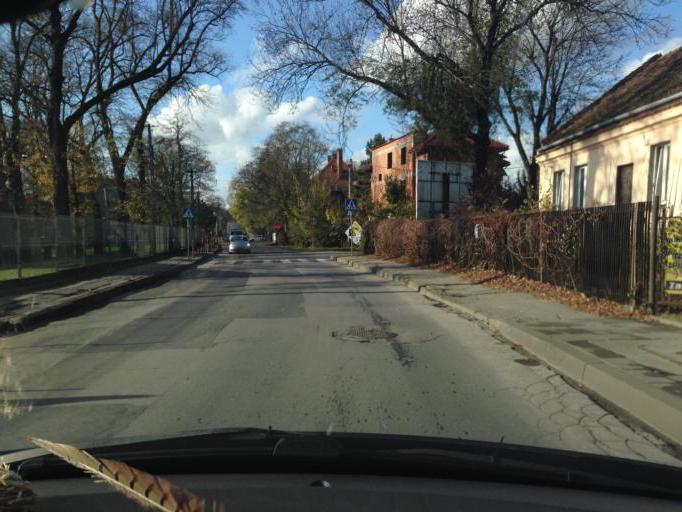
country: PL
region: Lesser Poland Voivodeship
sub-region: Powiat krakowski
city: Rzaska
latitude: 50.0645
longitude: 19.8819
